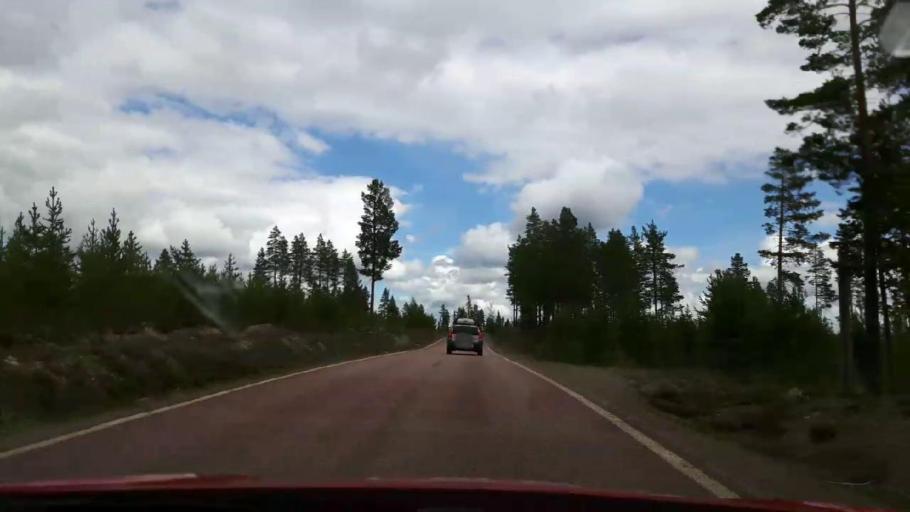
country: NO
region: Hedmark
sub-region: Trysil
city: Innbygda
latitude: 61.8686
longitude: 12.9577
